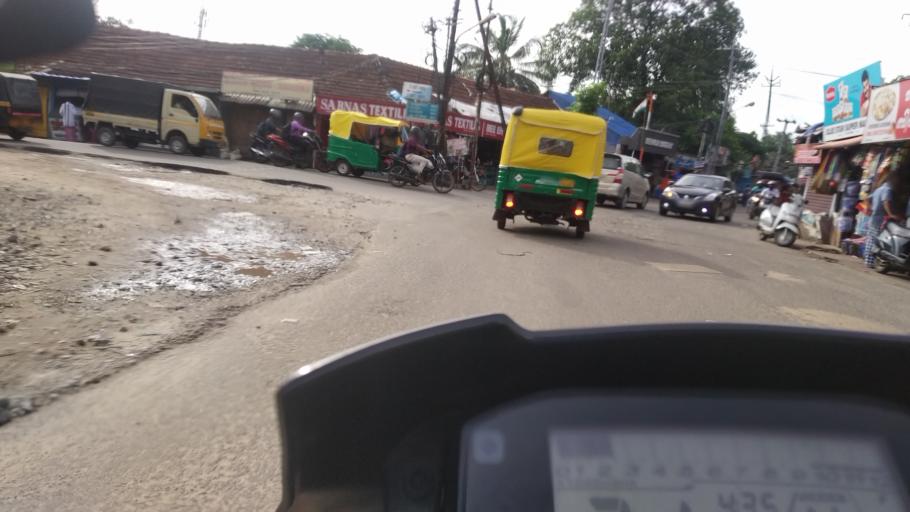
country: IN
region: Kerala
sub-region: Ernakulam
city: Cochin
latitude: 9.9863
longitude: 76.3109
